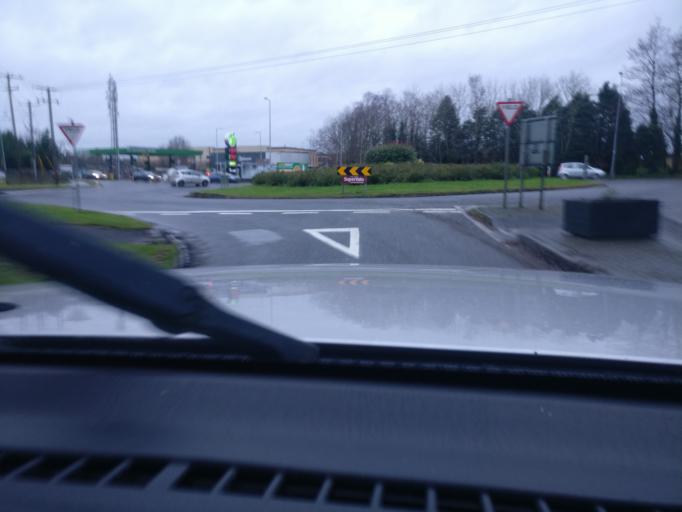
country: IE
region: Leinster
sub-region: An Mhi
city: Trim
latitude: 53.5474
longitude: -6.7934
